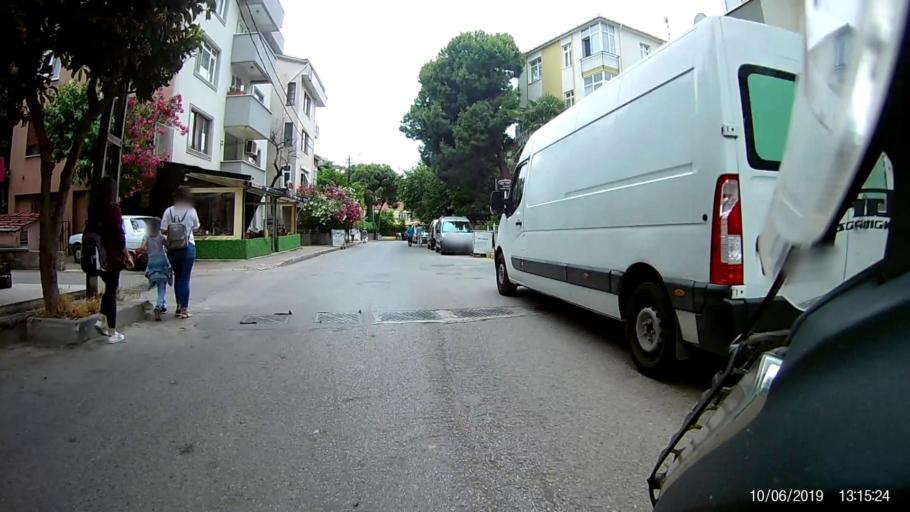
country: TR
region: Istanbul
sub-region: Atasehir
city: Atasehir
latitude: 40.9510
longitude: 29.1074
